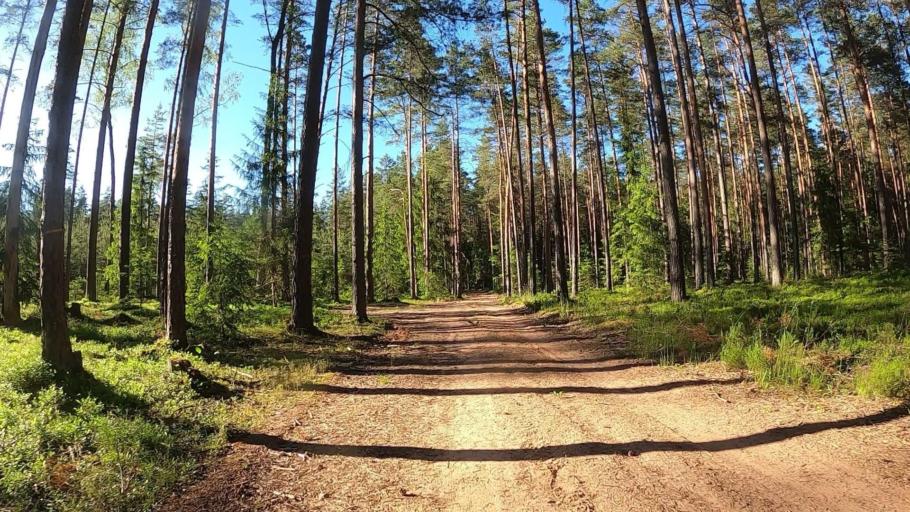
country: LV
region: Ogre
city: Ogre
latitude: 56.8395
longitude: 24.5896
